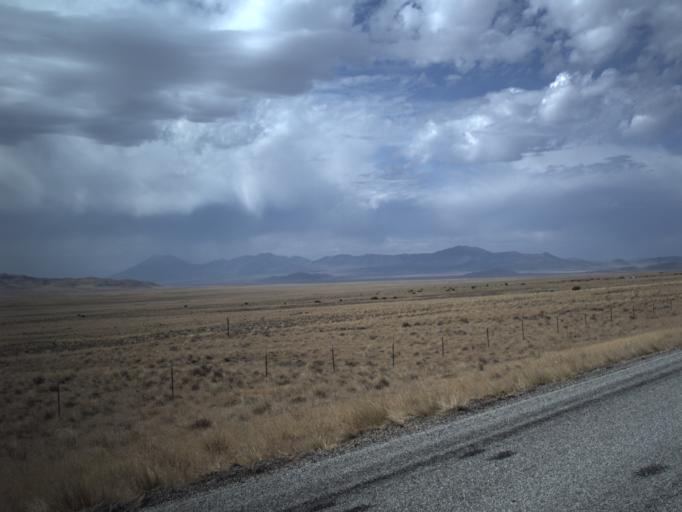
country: US
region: Utah
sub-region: Tooele County
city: Wendover
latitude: 41.4402
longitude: -113.7112
